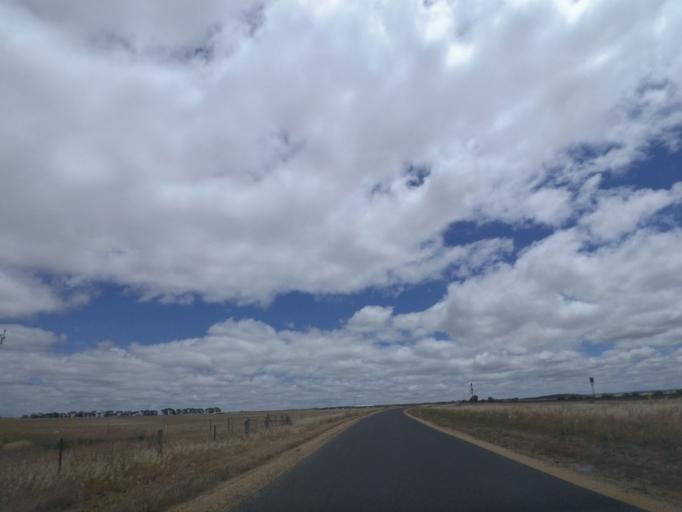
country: AU
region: Victoria
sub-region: Moorabool
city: Bacchus Marsh
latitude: -37.6837
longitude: 144.3573
